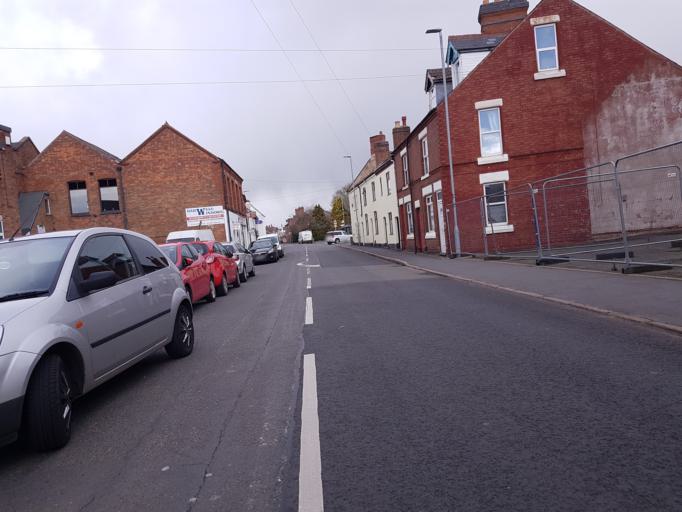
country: GB
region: England
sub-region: Leicestershire
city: Earl Shilton
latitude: 52.5644
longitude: -1.3493
